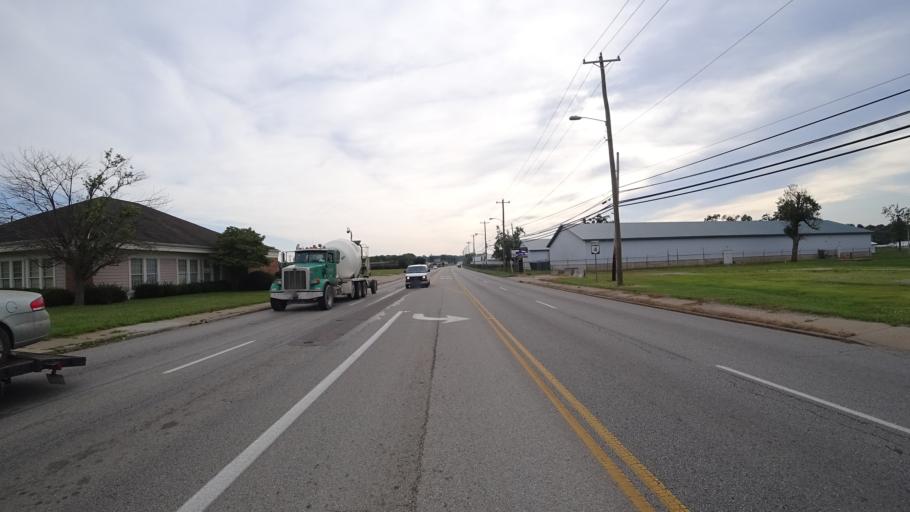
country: US
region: Ohio
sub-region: Butler County
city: Hamilton
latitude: 39.4019
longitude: -84.5403
